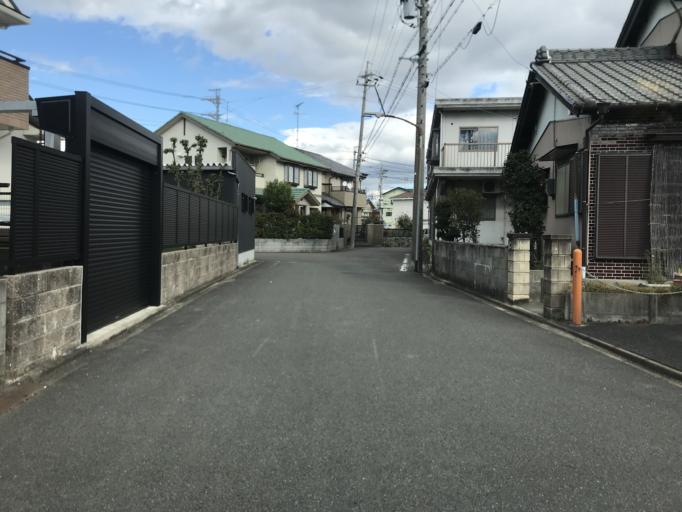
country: JP
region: Aichi
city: Nagoya-shi
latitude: 35.1944
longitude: 136.8443
